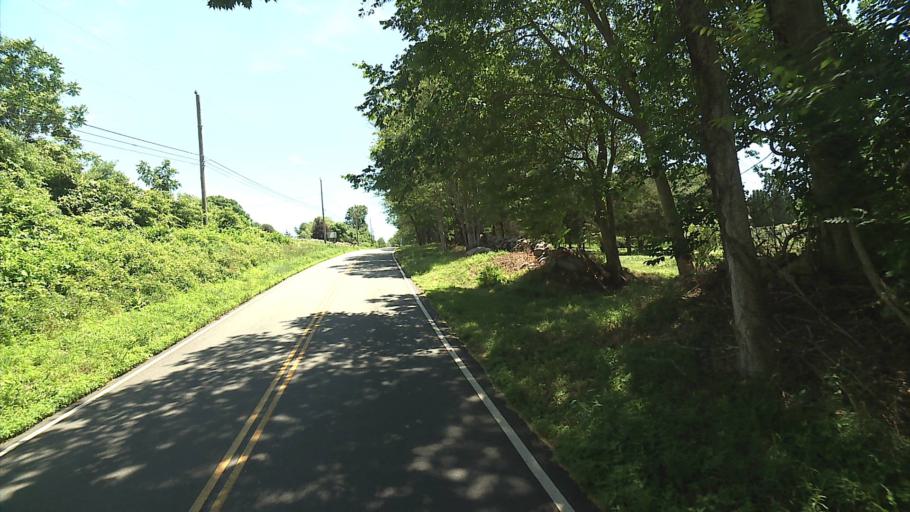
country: US
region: Connecticut
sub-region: New London County
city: Old Mystic
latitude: 41.3871
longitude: -71.9520
